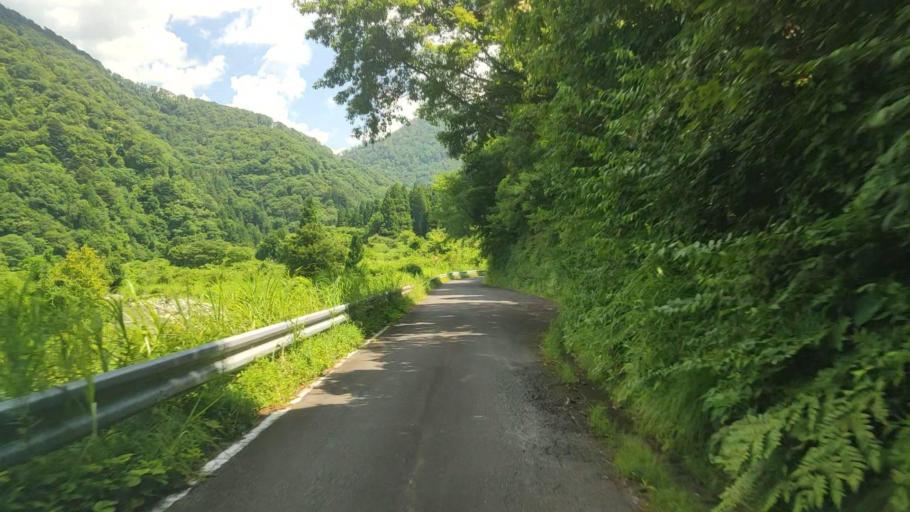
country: JP
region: Fukui
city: Ono
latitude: 35.7533
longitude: 136.5766
